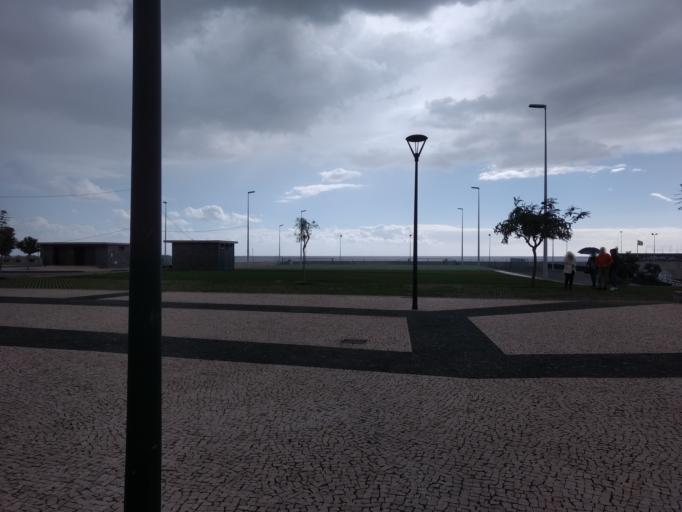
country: PT
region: Madeira
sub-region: Funchal
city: Funchal
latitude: 32.6468
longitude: -16.9067
